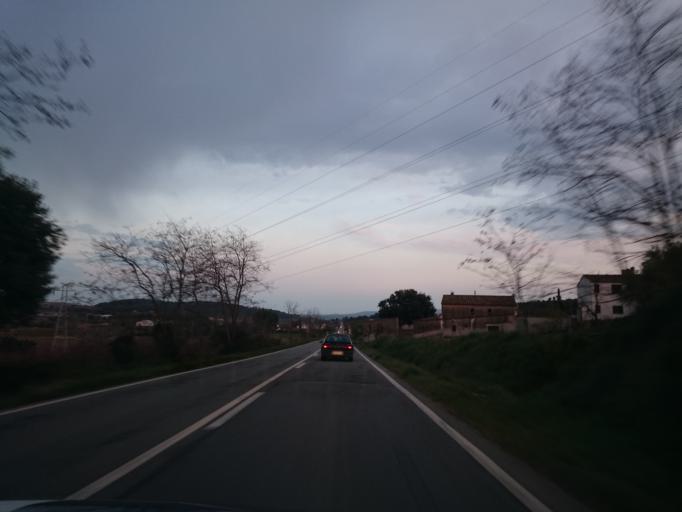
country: ES
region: Catalonia
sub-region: Provincia de Barcelona
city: Vilobi del Penedes
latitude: 41.3737
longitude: 1.6478
